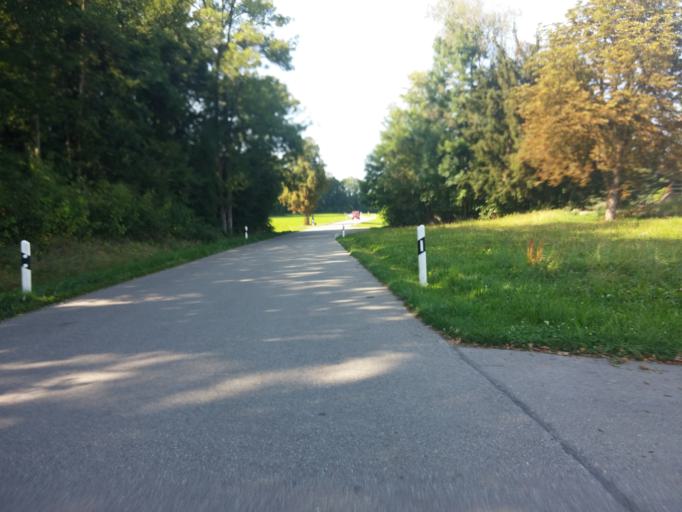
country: DE
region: Bavaria
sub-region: Swabia
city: Lautrach
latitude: 47.9093
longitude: 10.1240
